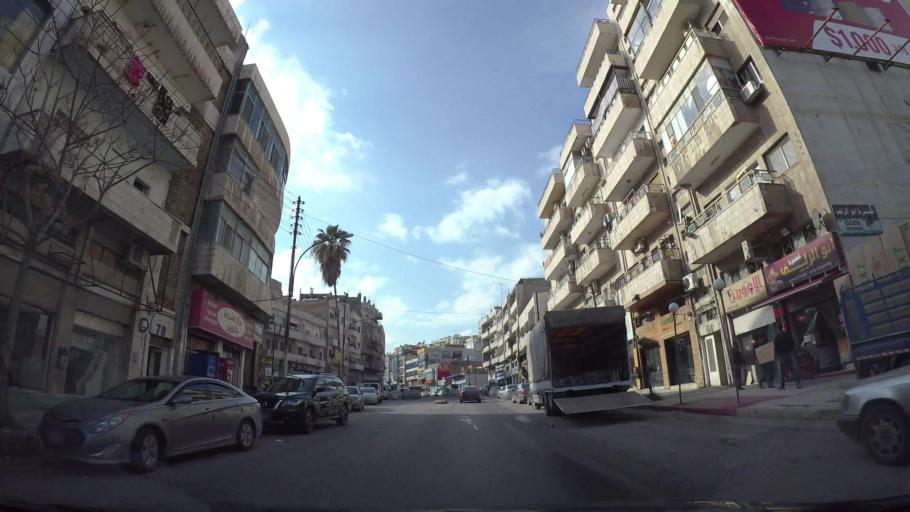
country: JO
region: Amman
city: Amman
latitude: 31.9561
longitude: 35.9149
